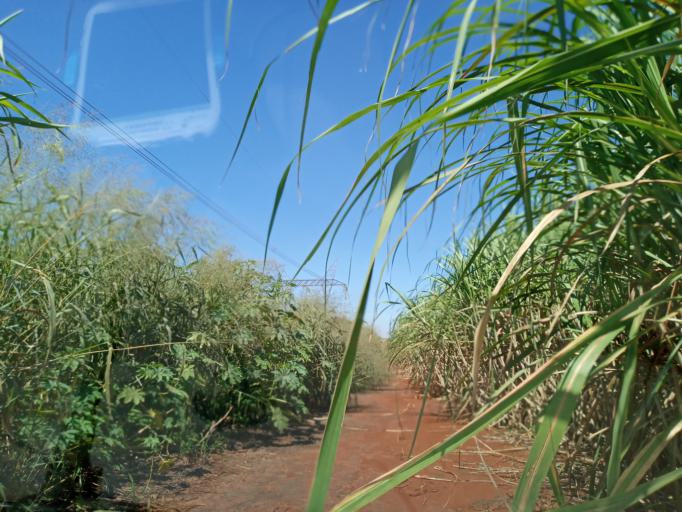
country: BR
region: Goias
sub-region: Itumbiara
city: Itumbiara
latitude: -18.4431
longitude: -49.1386
